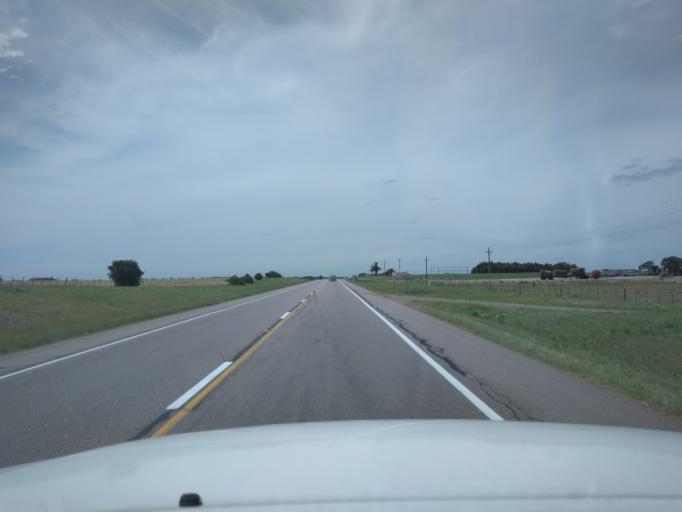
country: UY
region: Florida
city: Florida
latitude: -34.2286
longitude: -56.2119
